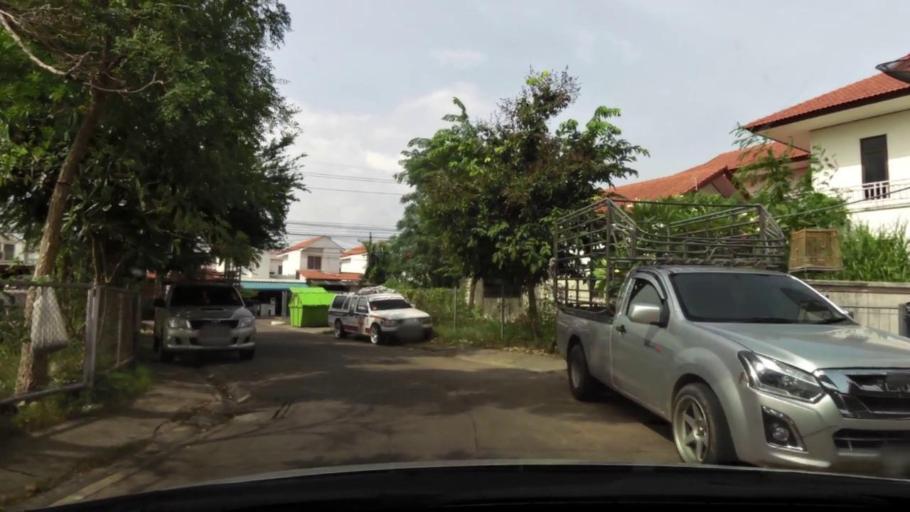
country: TH
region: Ratchaburi
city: Ratchaburi
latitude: 13.5382
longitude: 99.7935
